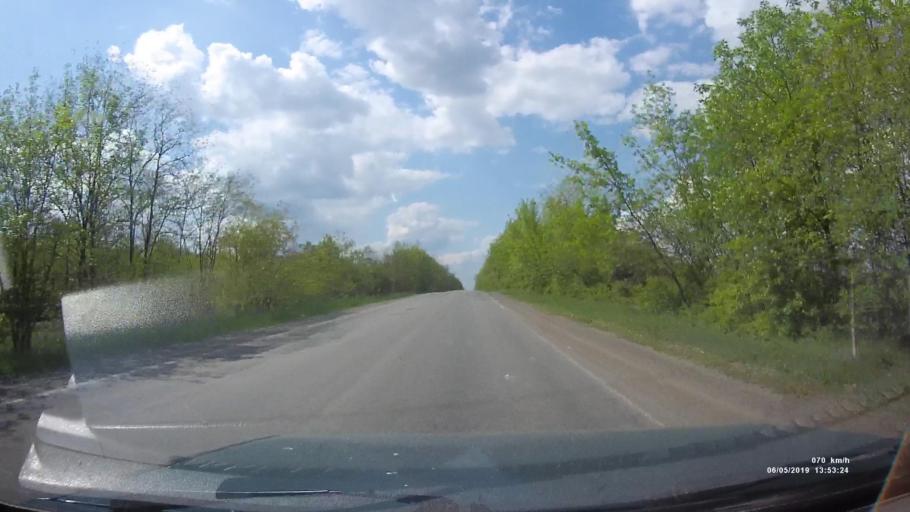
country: RU
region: Rostov
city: Melikhovskaya
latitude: 47.6680
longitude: 40.4629
